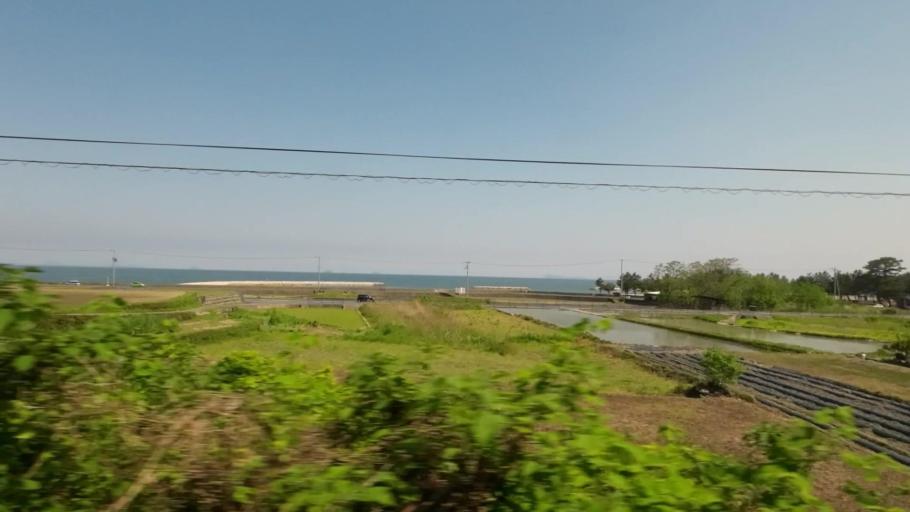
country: JP
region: Ehime
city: Kawanoecho
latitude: 33.9678
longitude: 133.4959
